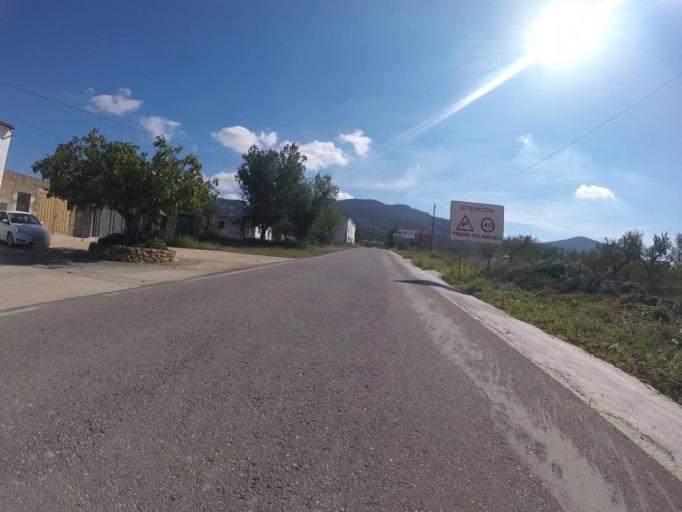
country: ES
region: Valencia
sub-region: Provincia de Castello
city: Sierra-Engarceran
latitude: 40.2981
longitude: -0.0469
